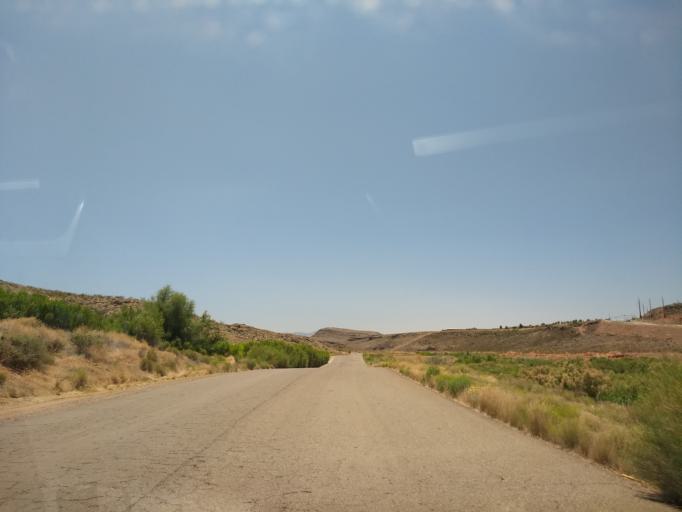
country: US
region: Utah
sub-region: Washington County
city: Washington
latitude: 37.1408
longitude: -113.4588
